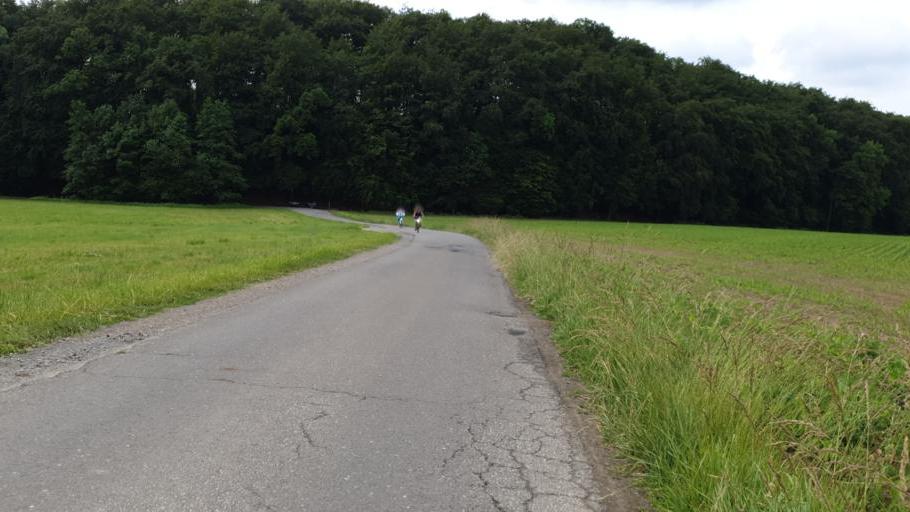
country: DE
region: North Rhine-Westphalia
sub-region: Regierungsbezirk Koln
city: Odenthal
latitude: 51.0257
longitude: 7.0997
